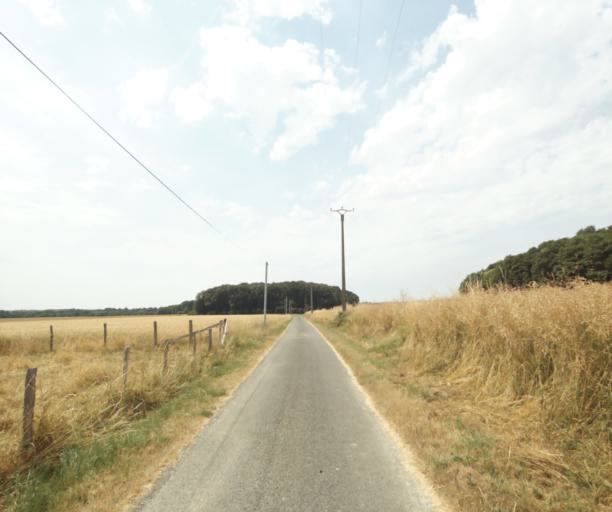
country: FR
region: Centre
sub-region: Departement d'Eure-et-Loir
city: La Bazoche-Gouet
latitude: 48.1899
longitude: 0.9509
